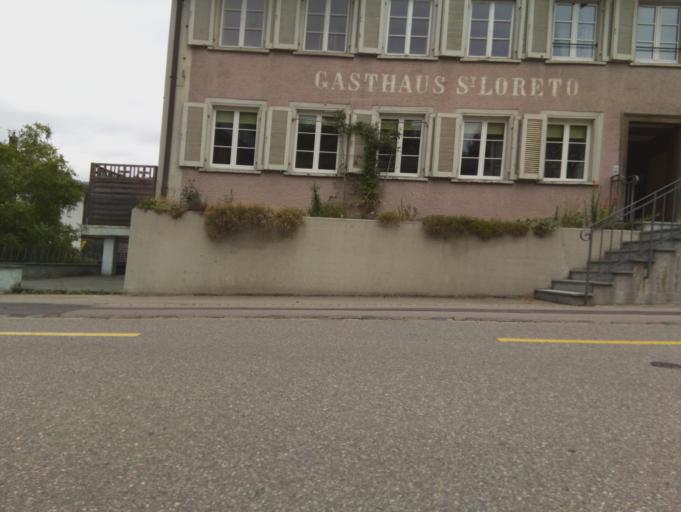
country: CH
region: Saint Gallen
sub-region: Wahlkreis Toggenburg
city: Lichtensteig
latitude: 47.3313
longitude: 9.0846
